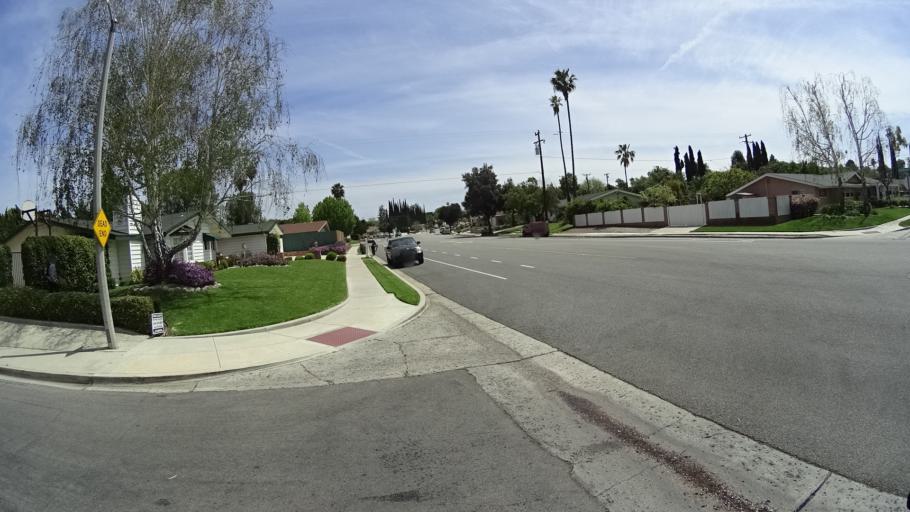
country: US
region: California
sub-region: Ventura County
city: Thousand Oaks
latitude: 34.1947
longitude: -118.8716
